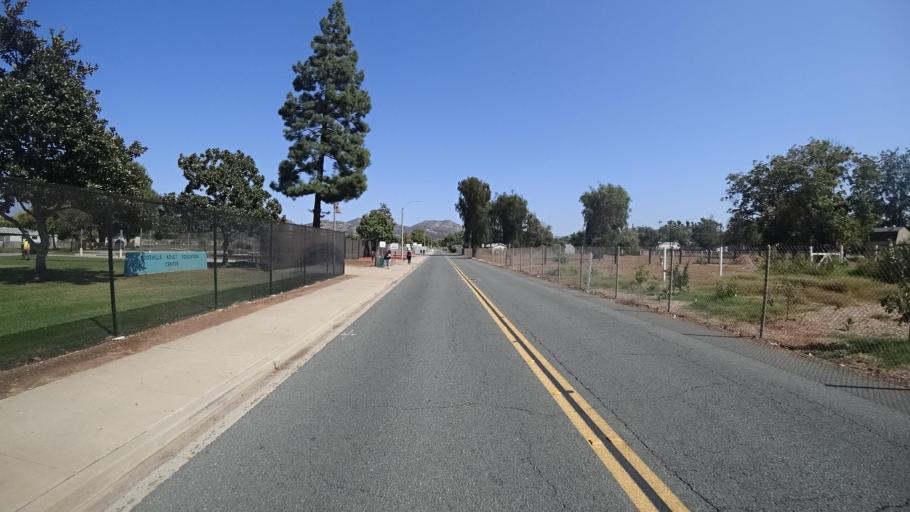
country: US
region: California
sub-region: San Diego County
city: Bostonia
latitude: 32.7965
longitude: -116.9242
